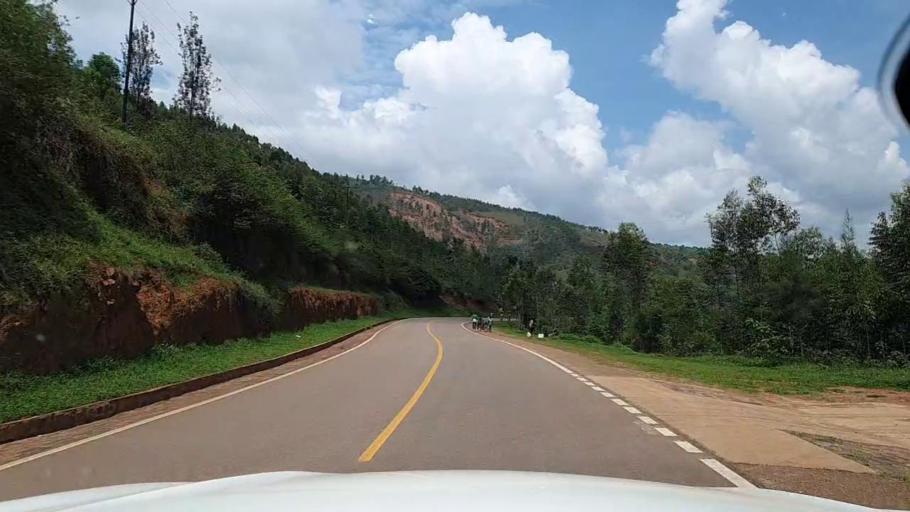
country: RW
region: Kigali
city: Kigali
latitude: -1.8380
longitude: 30.0824
